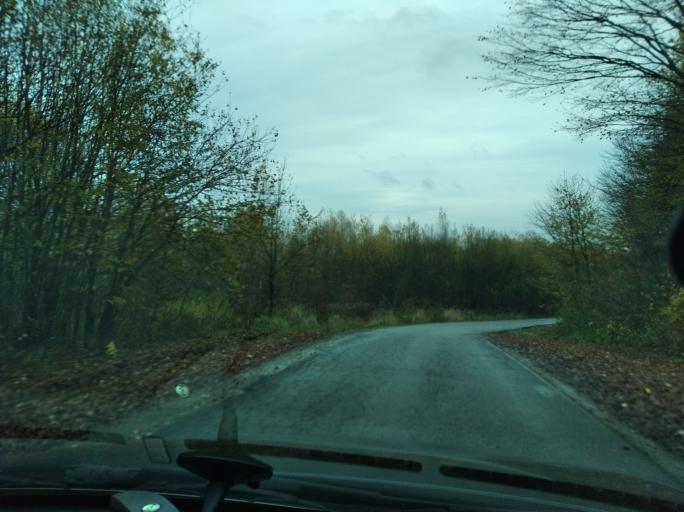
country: PL
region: Subcarpathian Voivodeship
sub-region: Powiat strzyzowski
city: Strzyzow
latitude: 49.9079
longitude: 21.7806
